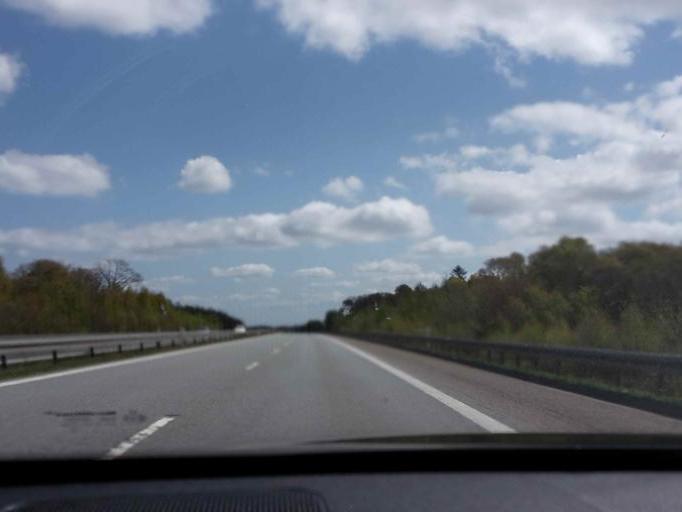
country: DK
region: South Denmark
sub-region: Vejen Kommune
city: Holsted
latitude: 55.5155
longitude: 8.9428
